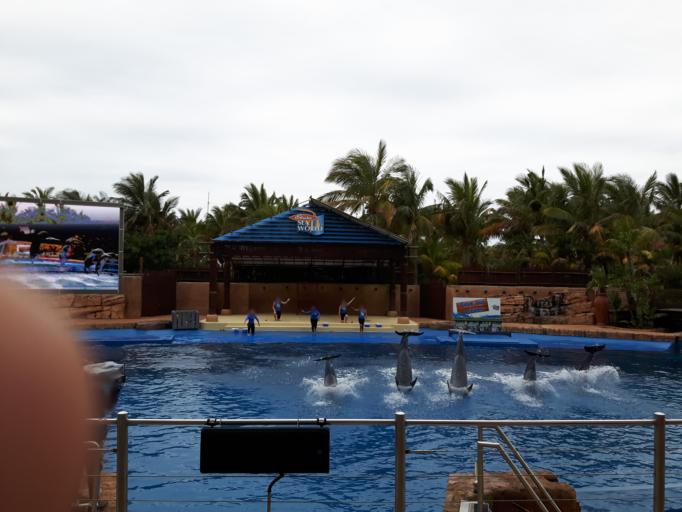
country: ZA
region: KwaZulu-Natal
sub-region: eThekwini Metropolitan Municipality
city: Durban
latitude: -29.8672
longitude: 31.0447
